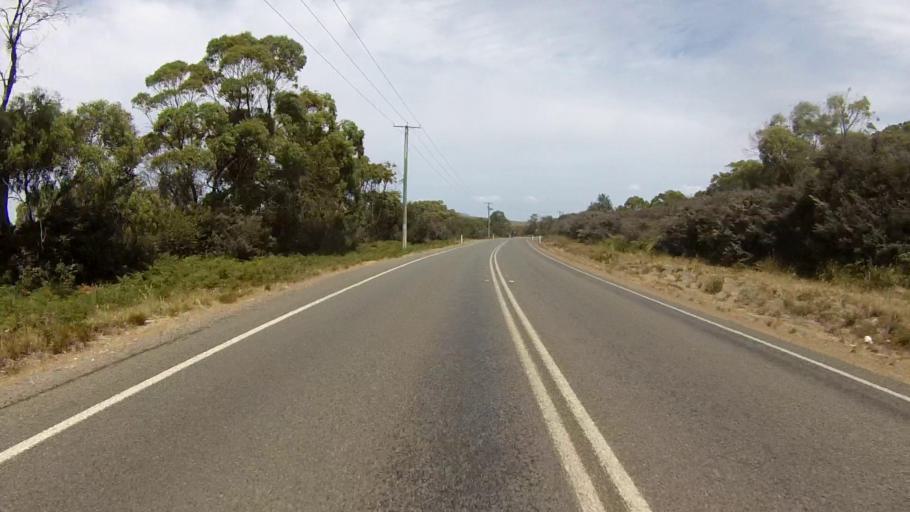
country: AU
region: Tasmania
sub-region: Clarence
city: Sandford
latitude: -43.0219
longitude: 147.4877
